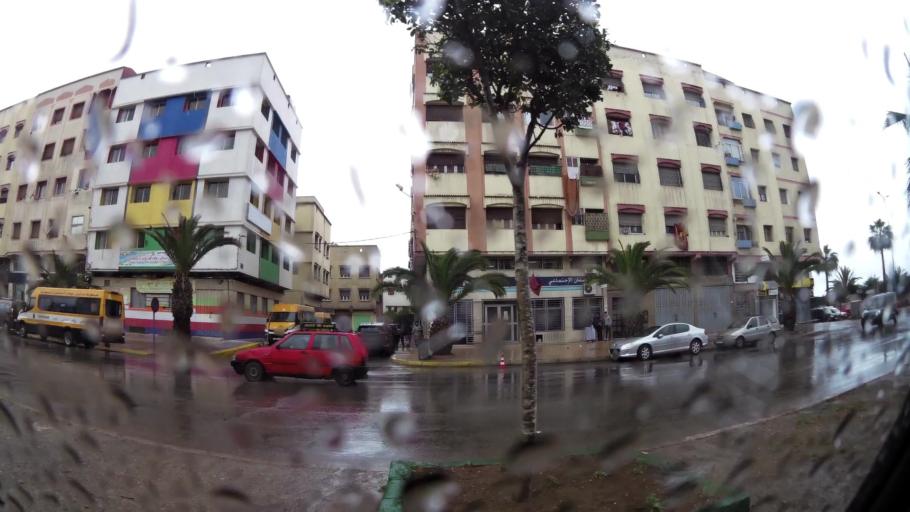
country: MA
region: Grand Casablanca
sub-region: Casablanca
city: Casablanca
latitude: 33.5438
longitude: -7.5620
